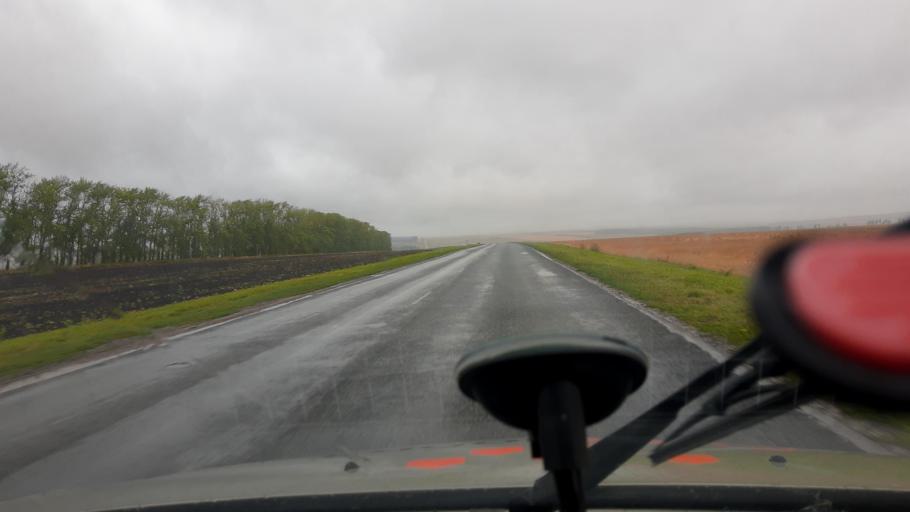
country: RU
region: Bashkortostan
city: Chekmagush
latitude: 55.0389
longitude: 54.6135
